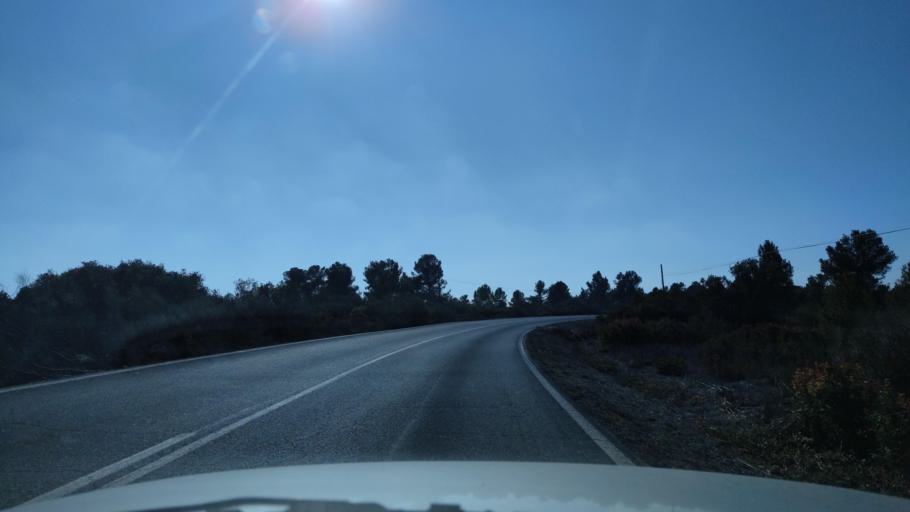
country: ES
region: Catalonia
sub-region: Provincia de Lleida
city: Maials
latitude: 41.3455
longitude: 0.4690
